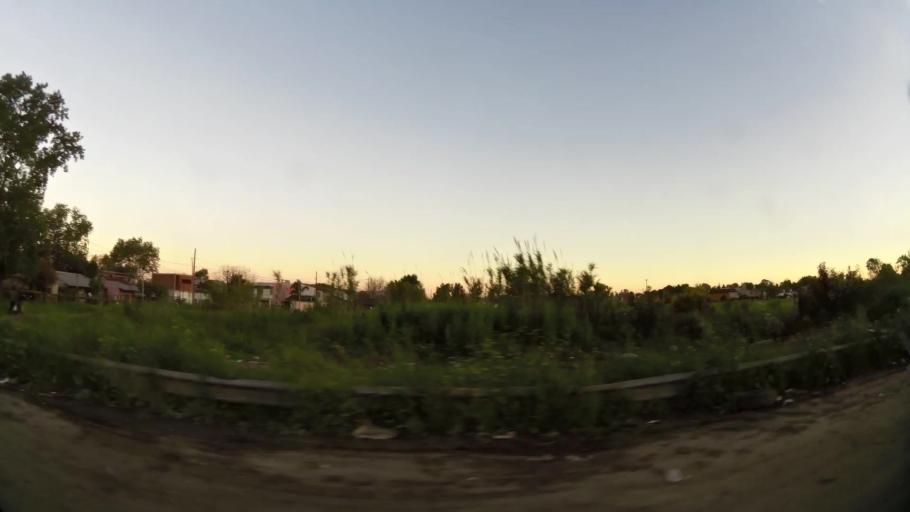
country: AR
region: Buenos Aires
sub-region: Partido de Almirante Brown
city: Adrogue
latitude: -34.8005
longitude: -58.3268
